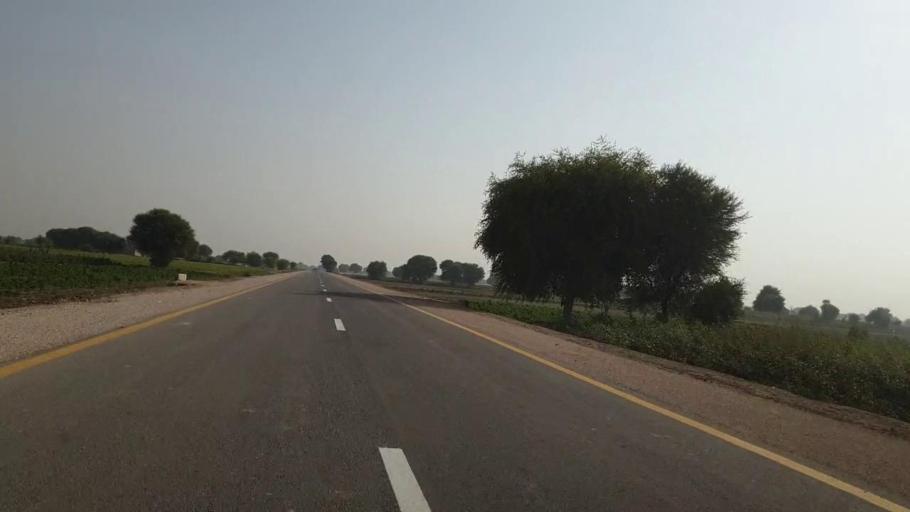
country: PK
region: Sindh
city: Bhan
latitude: 26.5306
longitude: 67.7889
